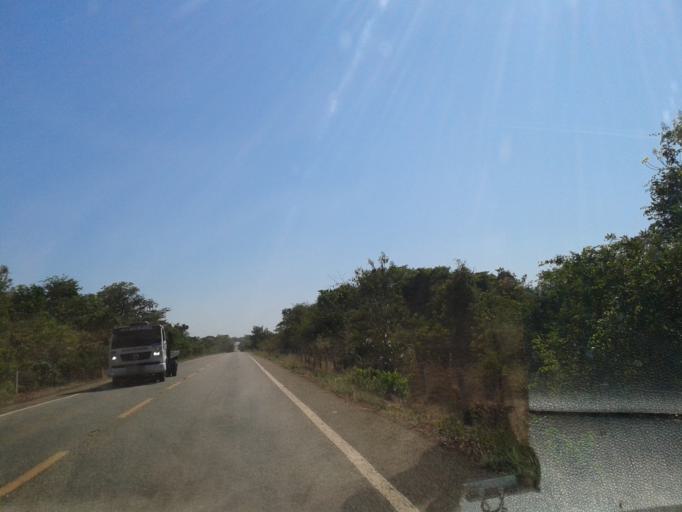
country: BR
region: Goias
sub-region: Crixas
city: Crixas
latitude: -14.0441
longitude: -50.3293
